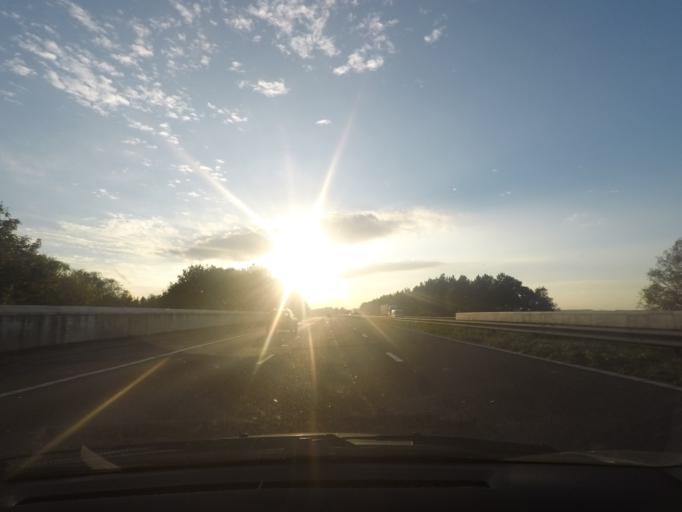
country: GB
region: England
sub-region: North Lincolnshire
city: Worlaby
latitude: 53.5777
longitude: -0.4554
